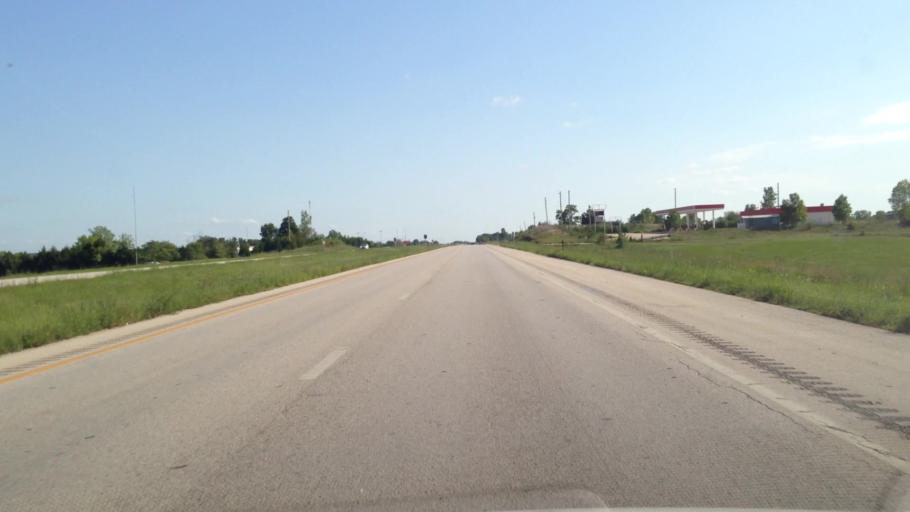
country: US
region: Kansas
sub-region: Bourbon County
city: Fort Scott
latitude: 37.7997
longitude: -94.7052
